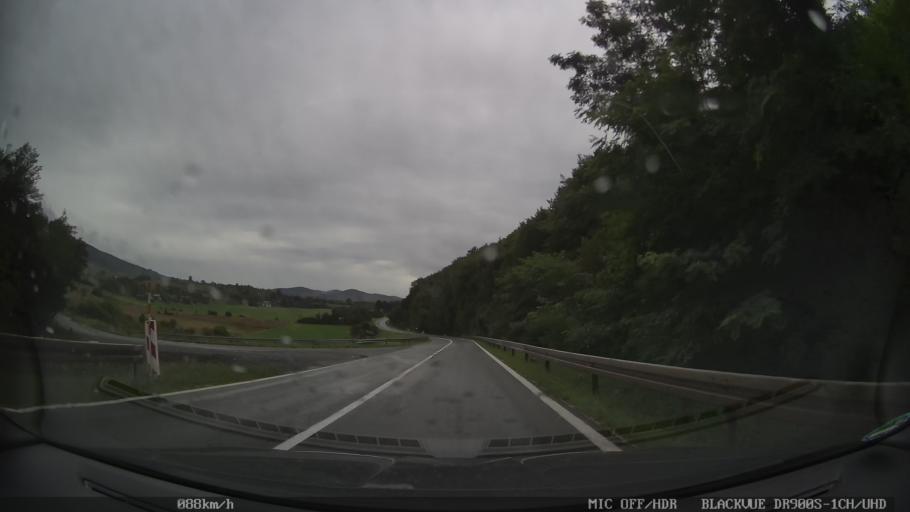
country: HR
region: Licko-Senjska
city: Brinje
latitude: 44.9596
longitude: 15.0930
